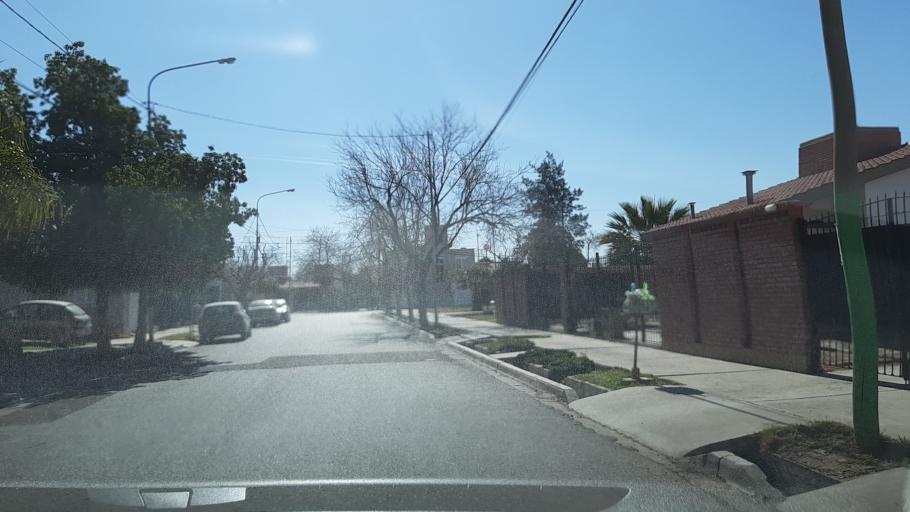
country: AR
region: San Juan
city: San Juan
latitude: -31.5378
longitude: -68.5818
